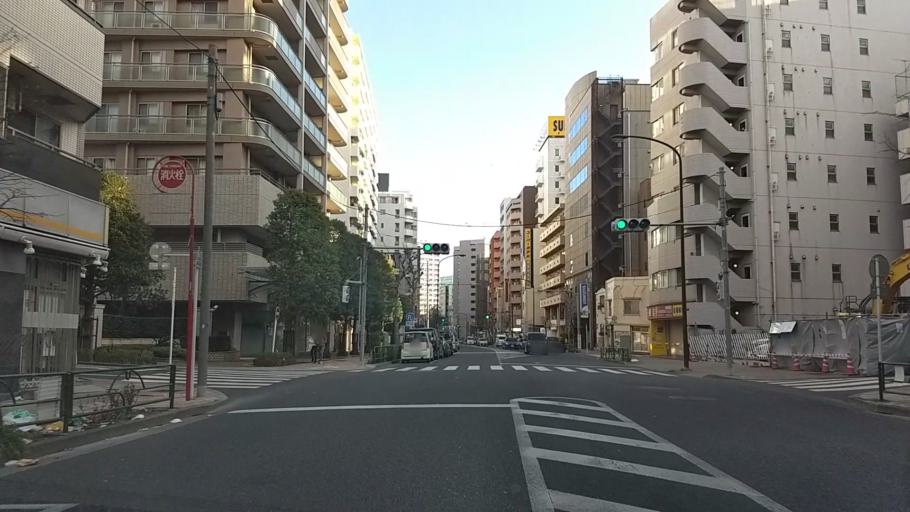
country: JP
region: Tokyo
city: Tokyo
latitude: 35.7346
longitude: 139.7274
